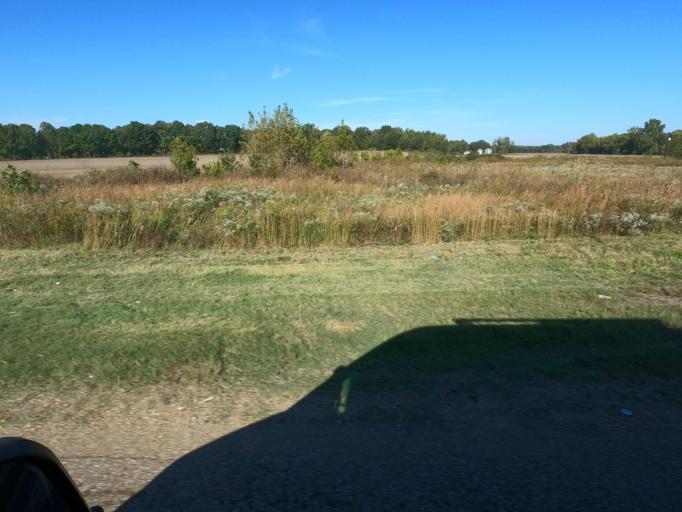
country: US
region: Tennessee
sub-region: Tipton County
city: Brighton
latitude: 35.5131
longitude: -89.7087
